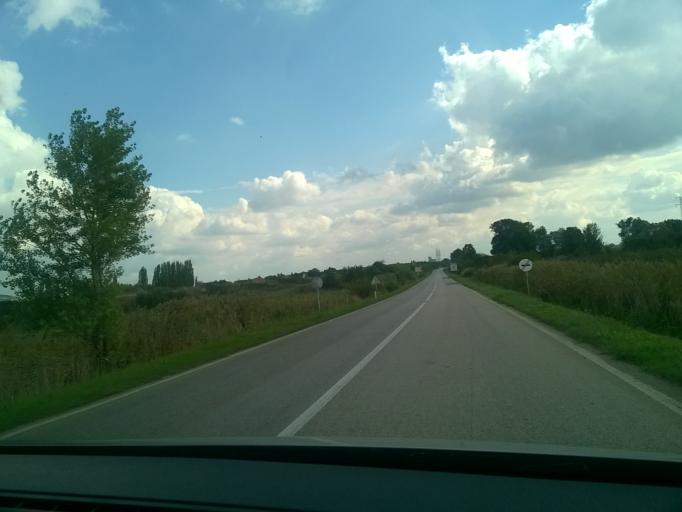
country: RS
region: Autonomna Pokrajina Vojvodina
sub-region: Juznobanatski Okrug
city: Vrsac
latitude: 45.1277
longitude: 21.2731
